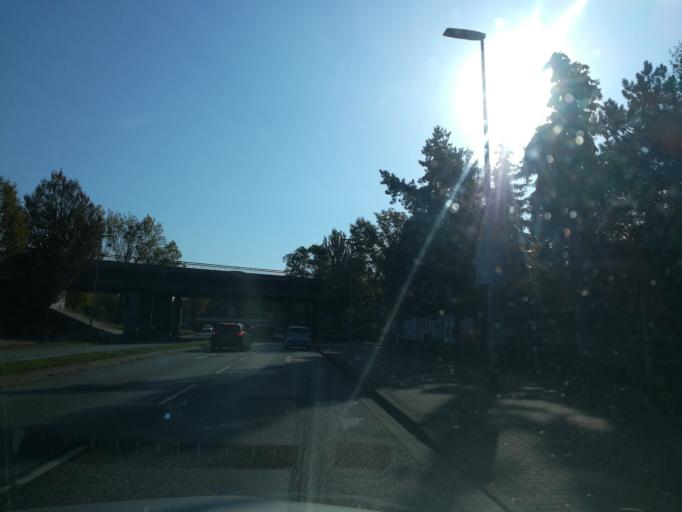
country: DE
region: Saxony-Anhalt
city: Neue Neustadt
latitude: 52.1405
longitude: 11.6281
